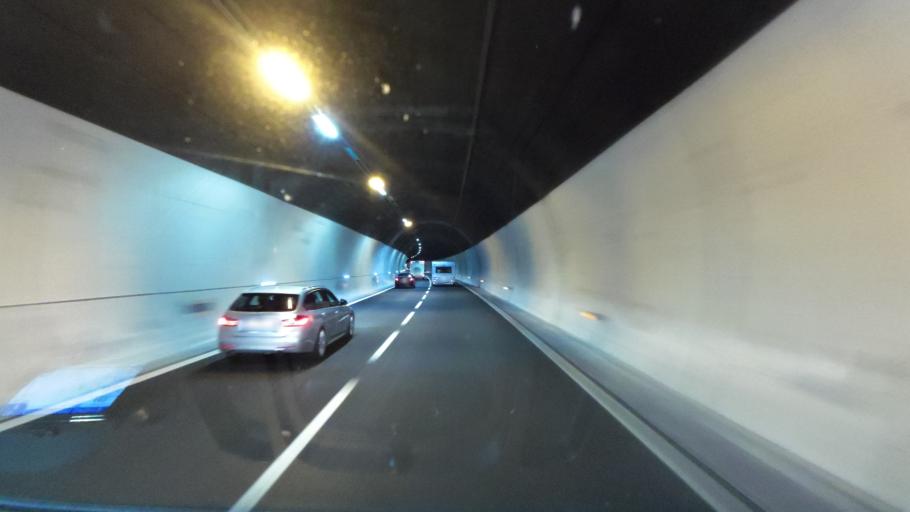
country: IT
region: Friuli Venezia Giulia
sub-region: Provincia di Udine
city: Moggio di Sotto
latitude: 46.3961
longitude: 13.1819
